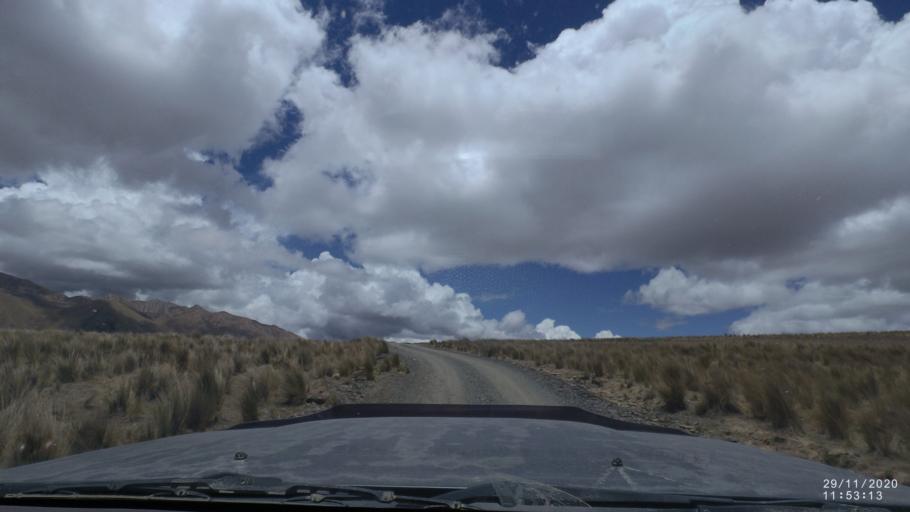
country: BO
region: Cochabamba
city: Cochabamba
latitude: -17.1656
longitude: -66.2678
